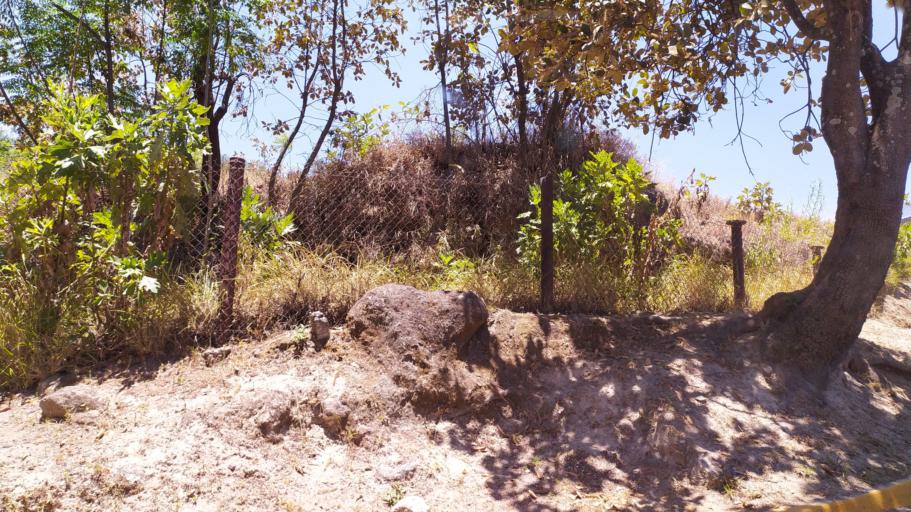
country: MX
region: Jalisco
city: Guadalajara
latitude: 20.6858
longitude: -103.4056
